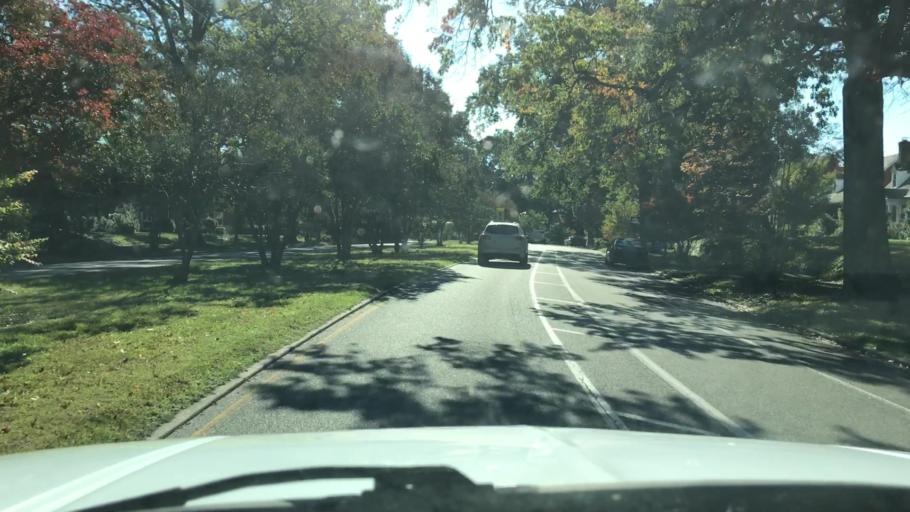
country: US
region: Virginia
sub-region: City of Richmond
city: Richmond
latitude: 37.5741
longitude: -77.4548
